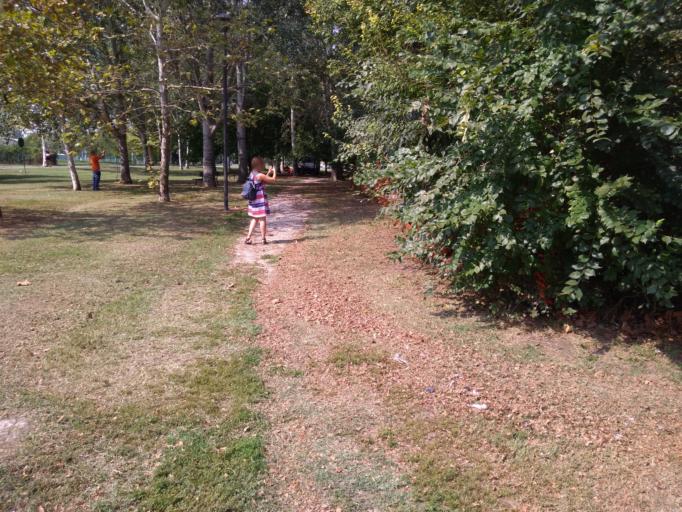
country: IT
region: Emilia-Romagna
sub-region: Provincia di Bologna
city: Quarto Inferiore
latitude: 44.5112
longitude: 11.3931
